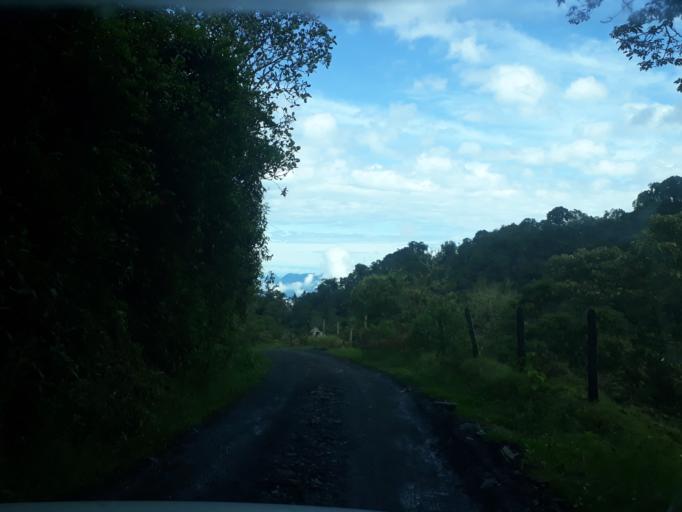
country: CO
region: Cundinamarca
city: Carmen de Carupa
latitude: 5.3440
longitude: -74.0536
